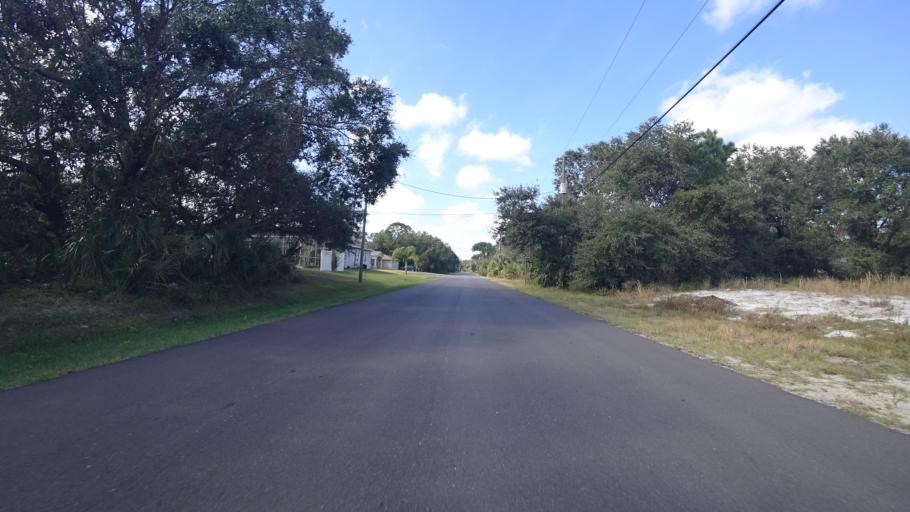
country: US
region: Florida
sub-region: Charlotte County
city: Port Charlotte
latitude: 27.0567
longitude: -82.1166
